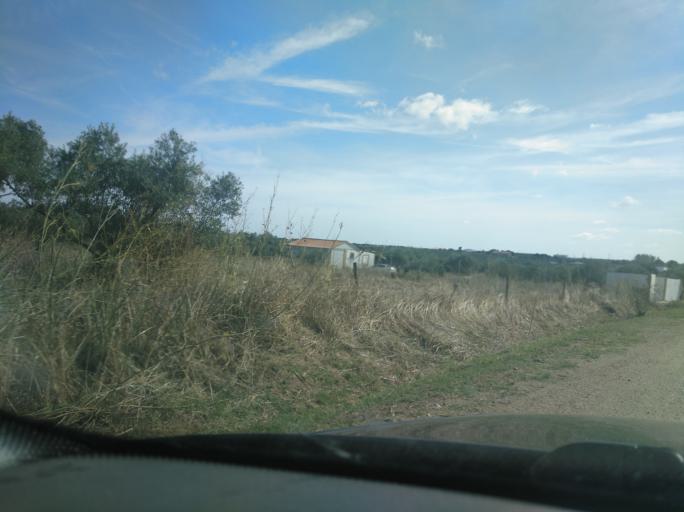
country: PT
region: Portalegre
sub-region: Campo Maior
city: Campo Maior
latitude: 39.0460
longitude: -7.0467
